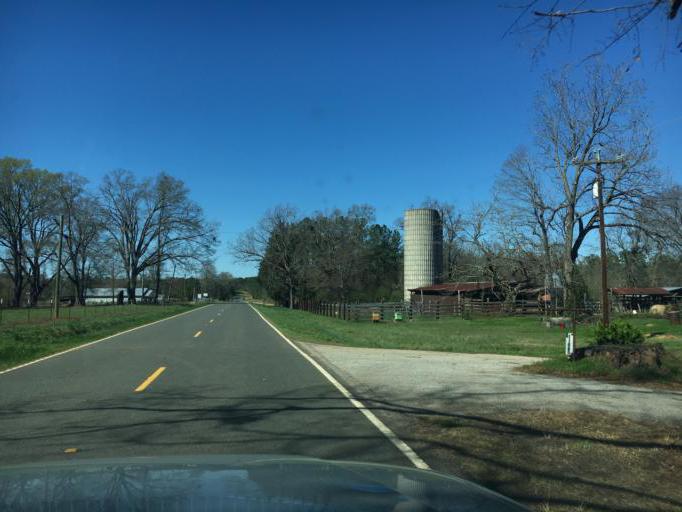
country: US
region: South Carolina
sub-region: Greenwood County
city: Ninety Six
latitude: 34.2821
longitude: -81.9523
